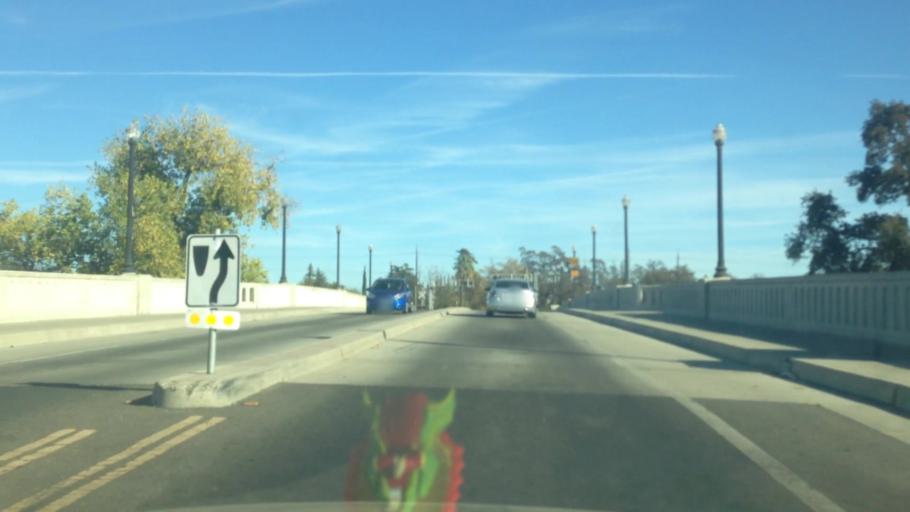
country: US
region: California
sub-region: Sacramento County
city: Sacramento
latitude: 38.6111
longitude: -121.4680
